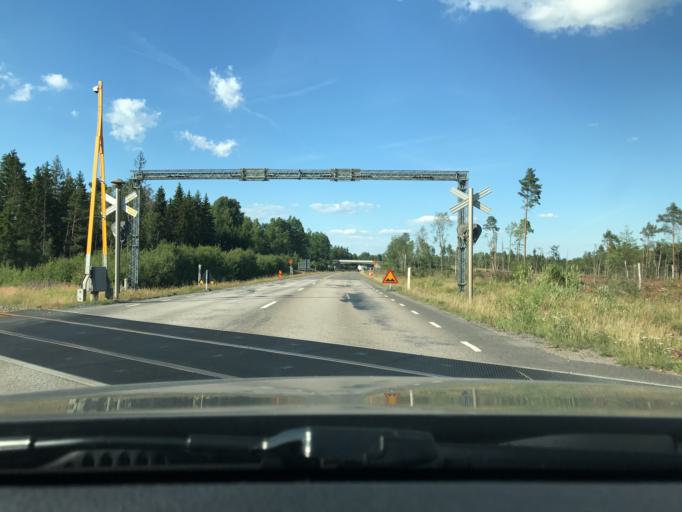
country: SE
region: Kronoberg
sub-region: Almhults Kommun
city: AElmhult
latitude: 56.5352
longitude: 14.1455
